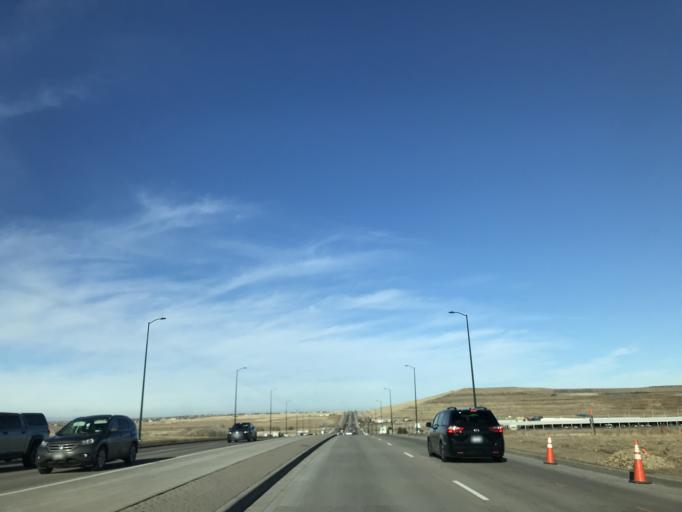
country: US
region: Colorado
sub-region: Adams County
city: Aurora
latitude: 39.8386
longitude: -104.7718
